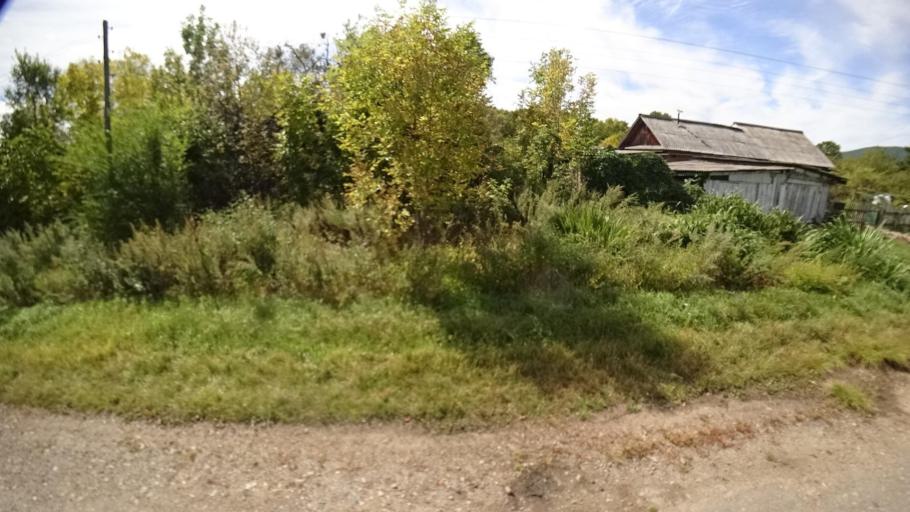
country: RU
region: Primorskiy
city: Yakovlevka
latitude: 44.6542
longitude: 133.7461
